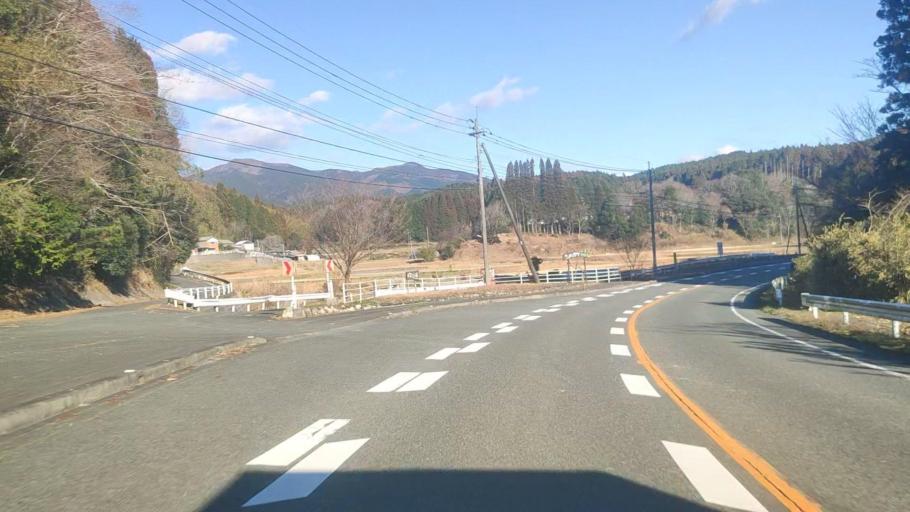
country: JP
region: Fukuoka
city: Maebaru-chuo
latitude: 33.4369
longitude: 130.2667
